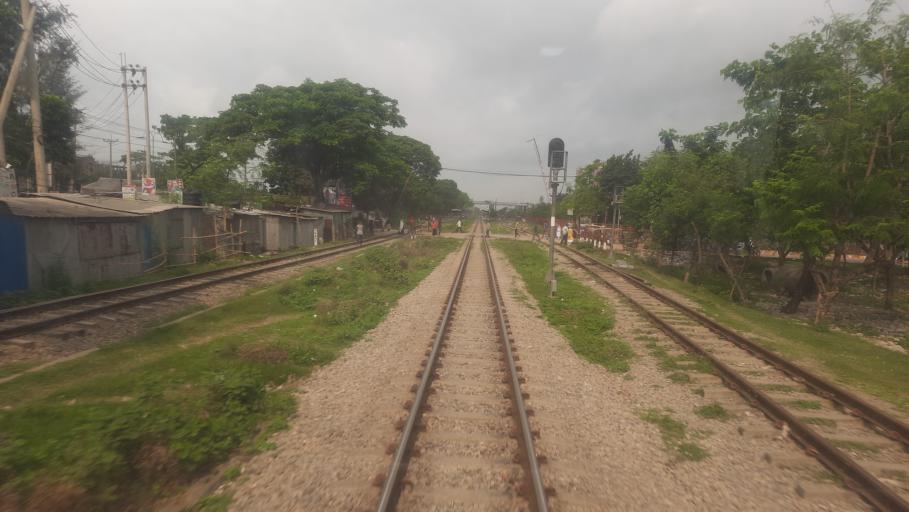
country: BD
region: Dhaka
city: Narsingdi
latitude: 23.9313
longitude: 90.7252
